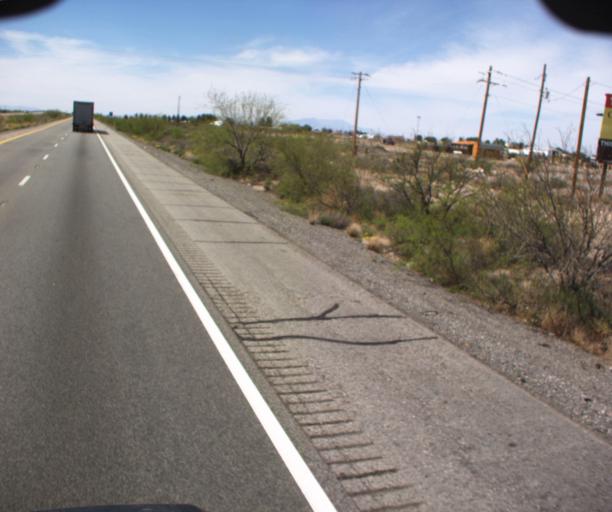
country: US
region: New Mexico
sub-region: Hidalgo County
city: Lordsburg
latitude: 32.2614
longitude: -109.2190
